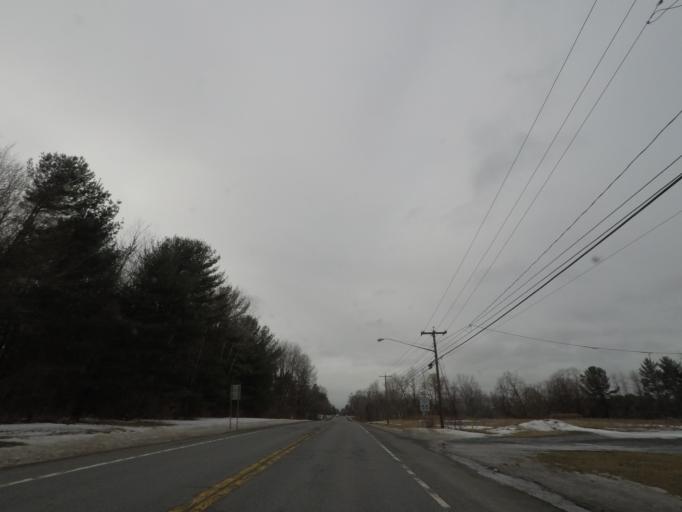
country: US
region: New York
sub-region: Albany County
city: Voorheesville
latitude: 42.7207
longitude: -73.9462
